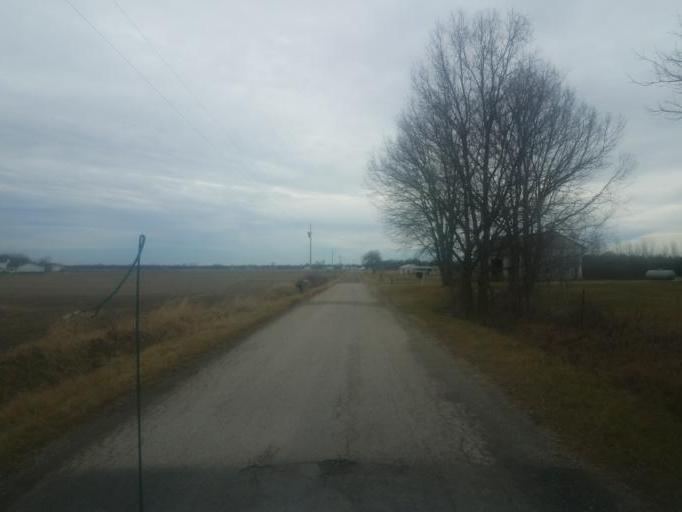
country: US
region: Ohio
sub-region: Morrow County
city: Mount Gilead
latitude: 40.6262
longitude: -82.9127
